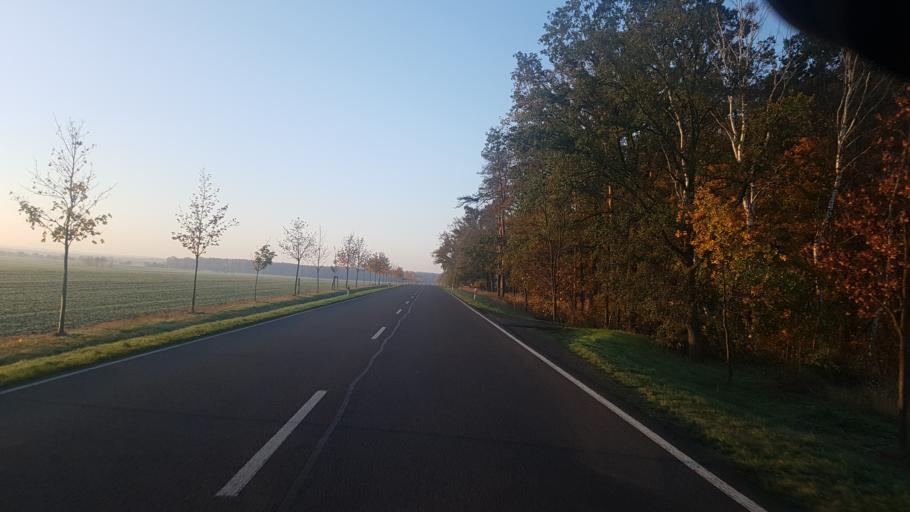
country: DE
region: Saxony
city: Torgau
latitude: 51.4928
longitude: 12.9898
